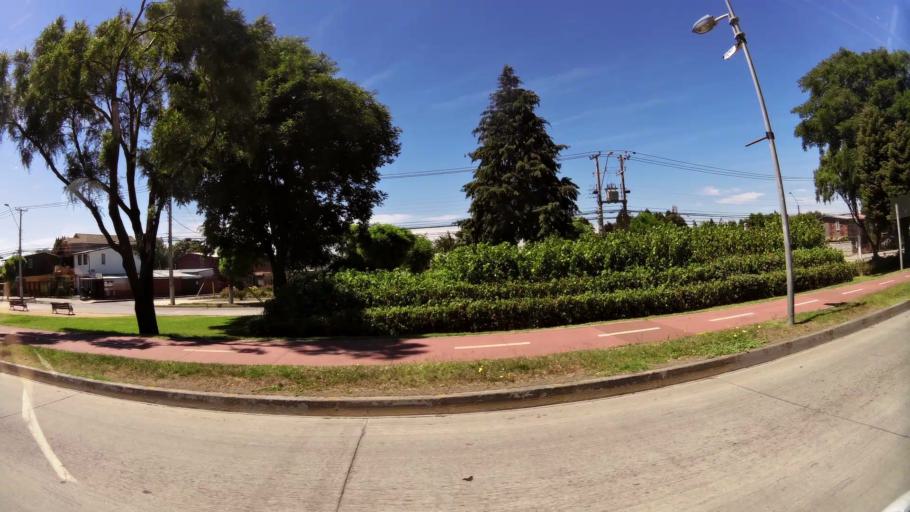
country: CL
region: Biobio
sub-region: Provincia de Concepcion
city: Talcahuano
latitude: -36.7580
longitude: -73.0904
